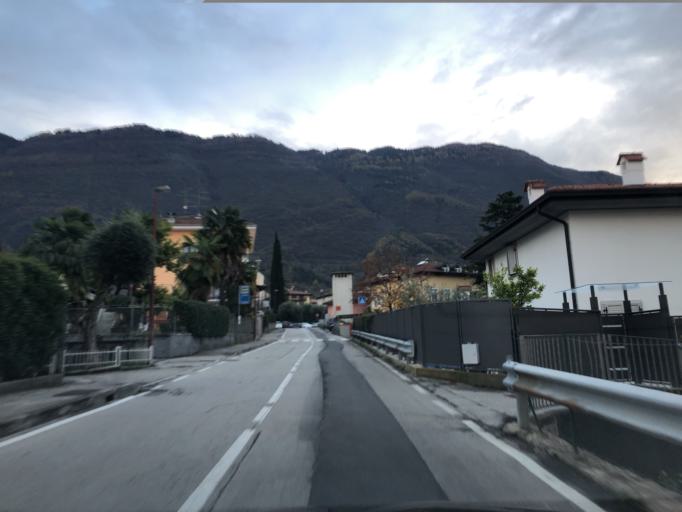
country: IT
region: Trentino-Alto Adige
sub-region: Provincia di Trento
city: Bolognano-Vignole
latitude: 45.9144
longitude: 10.9018
